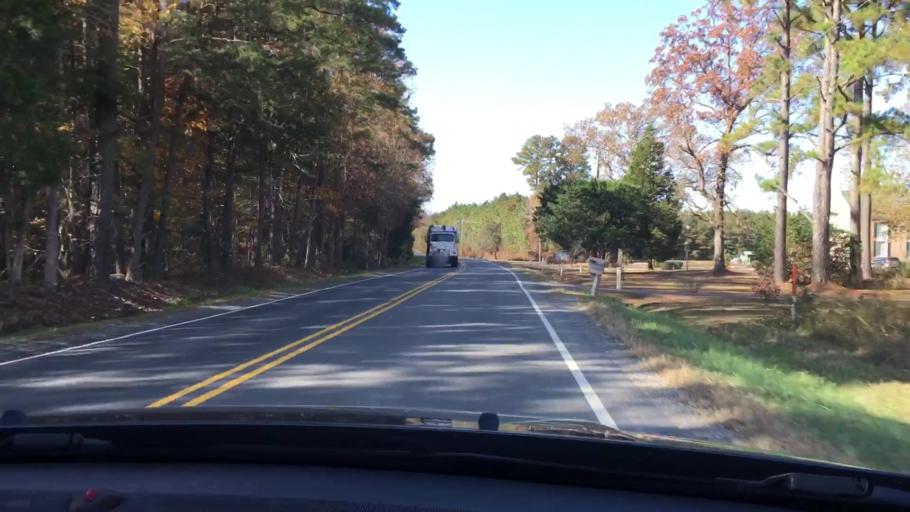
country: US
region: Virginia
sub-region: King William County
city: King William
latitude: 37.6570
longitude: -76.9506
